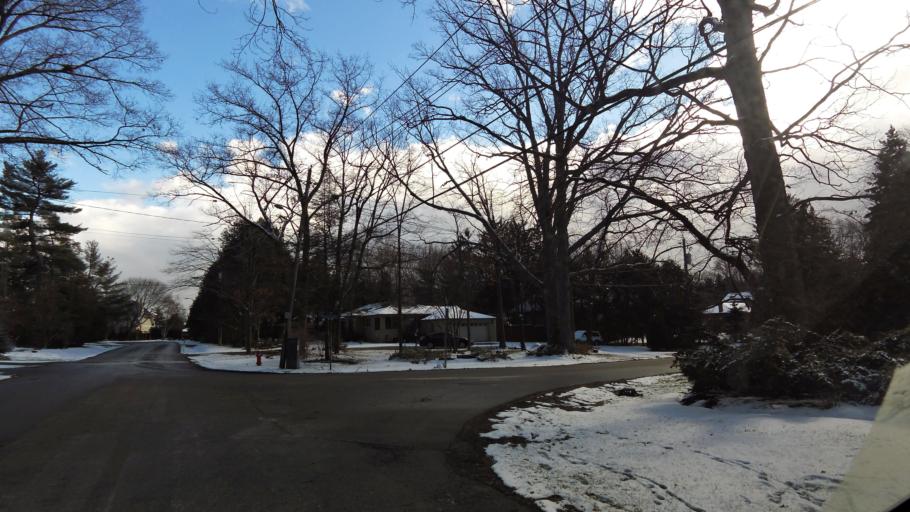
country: CA
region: Ontario
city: Mississauga
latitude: 43.5676
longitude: -79.6058
